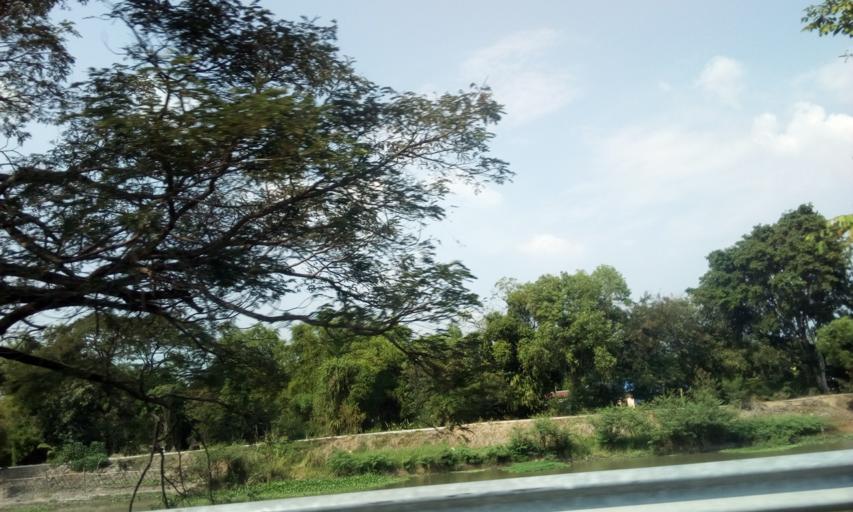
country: TH
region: Nakhon Nayok
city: Ban Na
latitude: 14.2074
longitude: 101.0710
